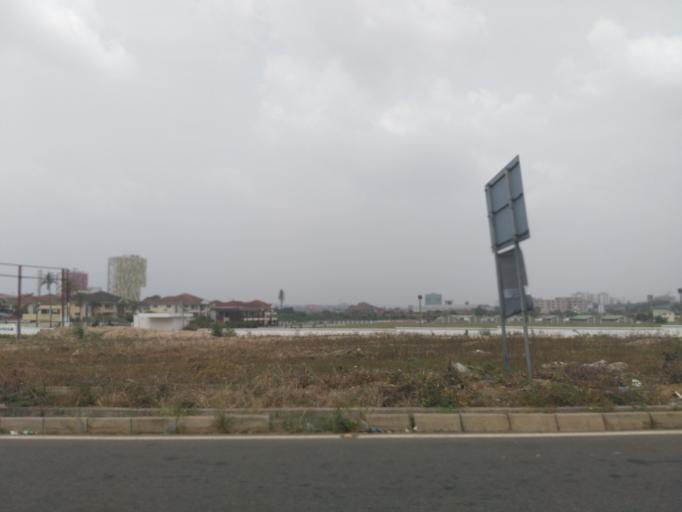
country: GH
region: Greater Accra
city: Medina Estates
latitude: 5.6143
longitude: -0.1735
